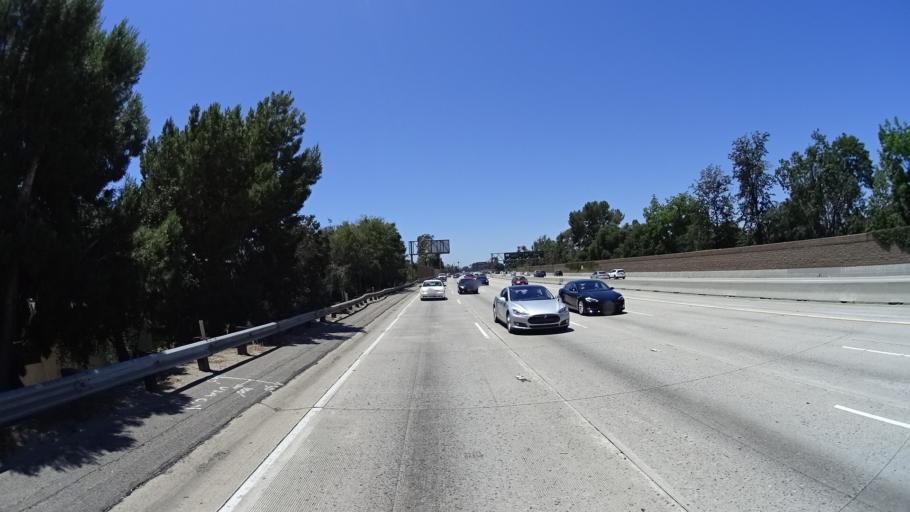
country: US
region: California
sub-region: Los Angeles County
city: Universal City
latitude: 34.1527
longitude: -118.3549
